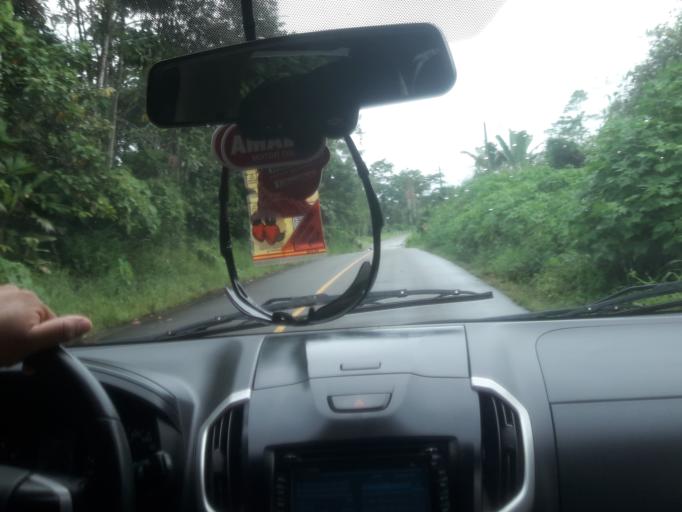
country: EC
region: Napo
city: Tena
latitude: -1.0341
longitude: -77.6877
